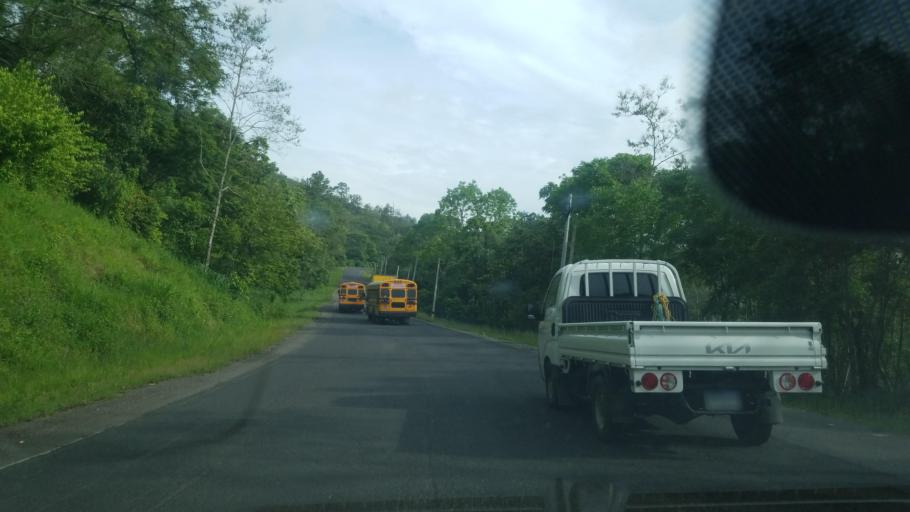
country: HN
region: Santa Barbara
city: Petoa
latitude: 15.2068
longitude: -88.2697
